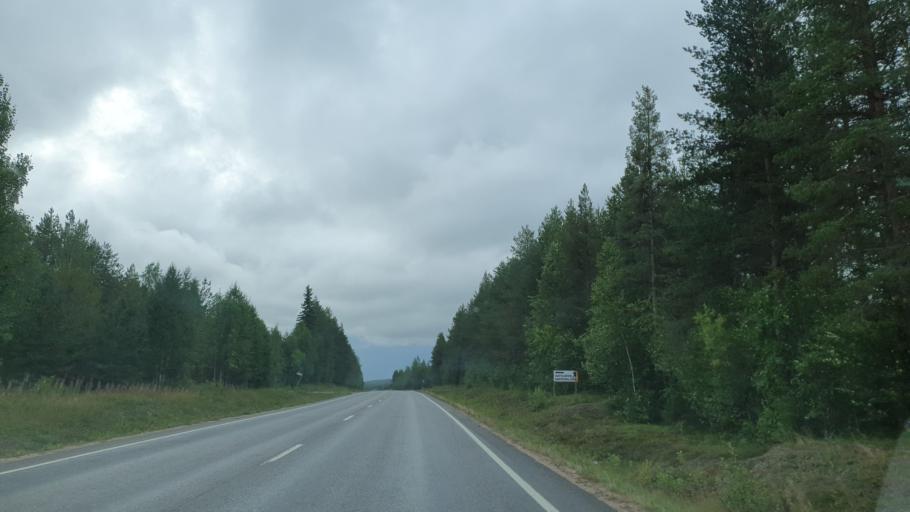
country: FI
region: Lapland
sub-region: Tunturi-Lappi
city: Kolari
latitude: 67.2115
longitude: 23.9054
